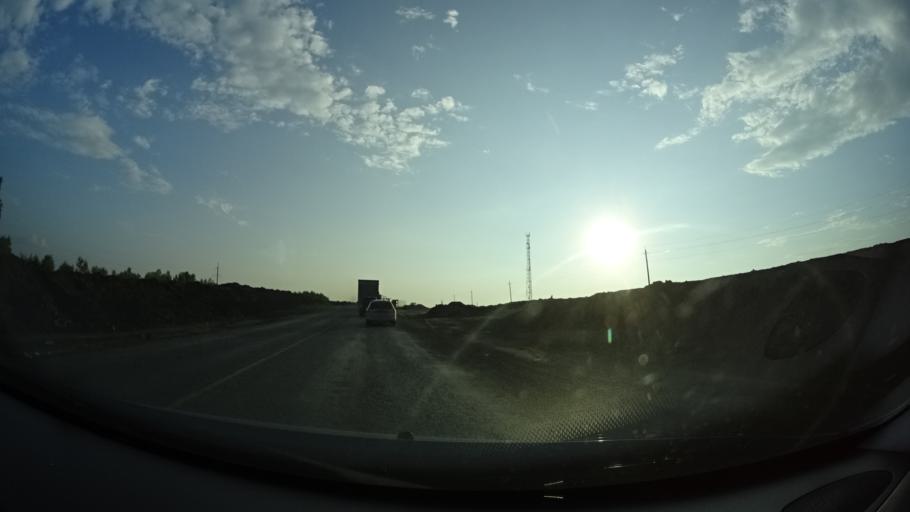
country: RU
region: Samara
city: Kamyshla
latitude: 54.0450
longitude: 52.0028
